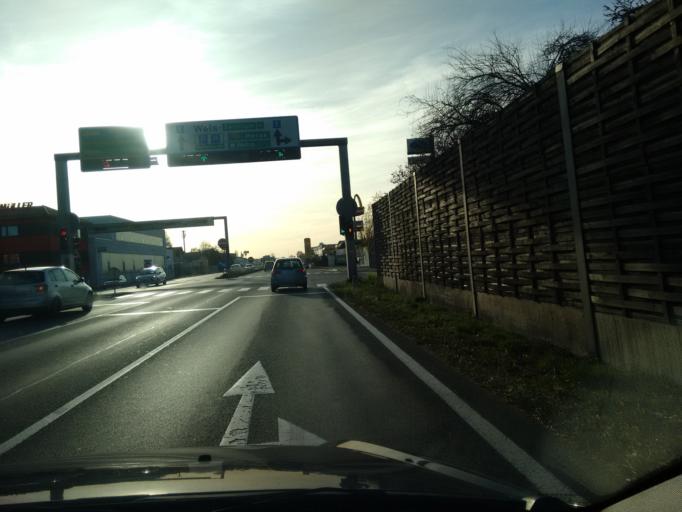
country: AT
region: Upper Austria
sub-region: Wels Stadt
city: Wels
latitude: 48.1802
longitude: 14.0645
